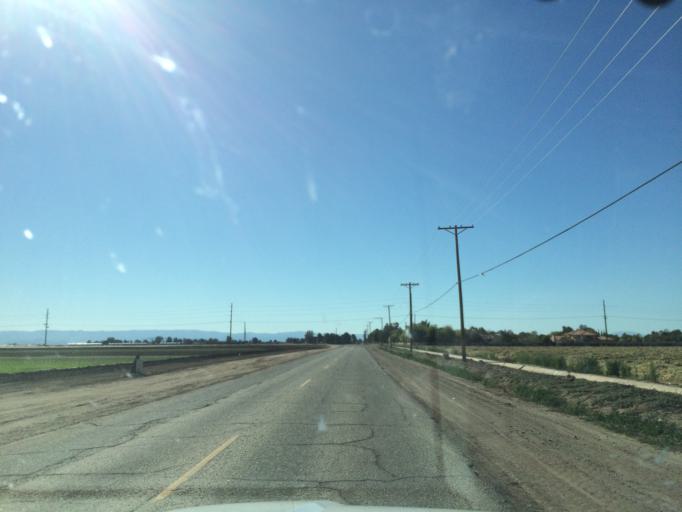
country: US
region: California
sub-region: Imperial County
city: Heber
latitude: 32.7524
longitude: -115.5407
